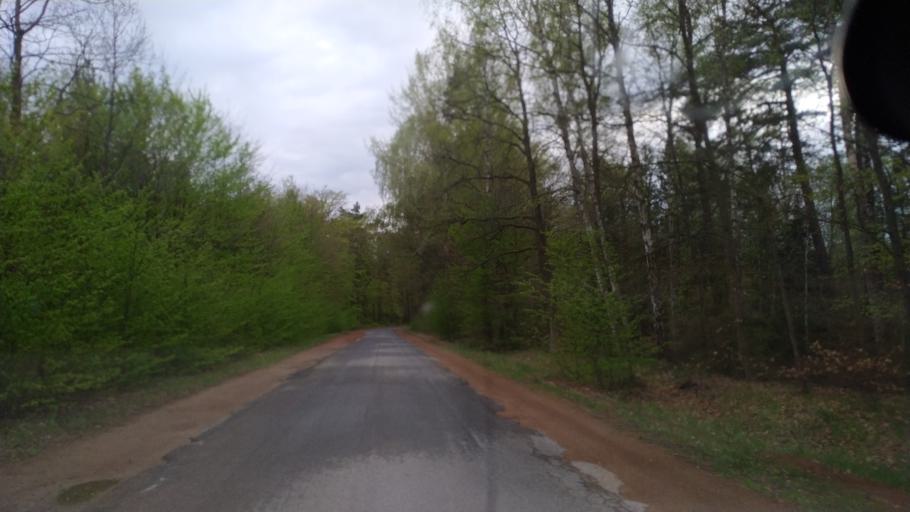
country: PL
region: Pomeranian Voivodeship
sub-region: Powiat starogardzki
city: Osiek
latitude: 53.7018
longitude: 18.5695
